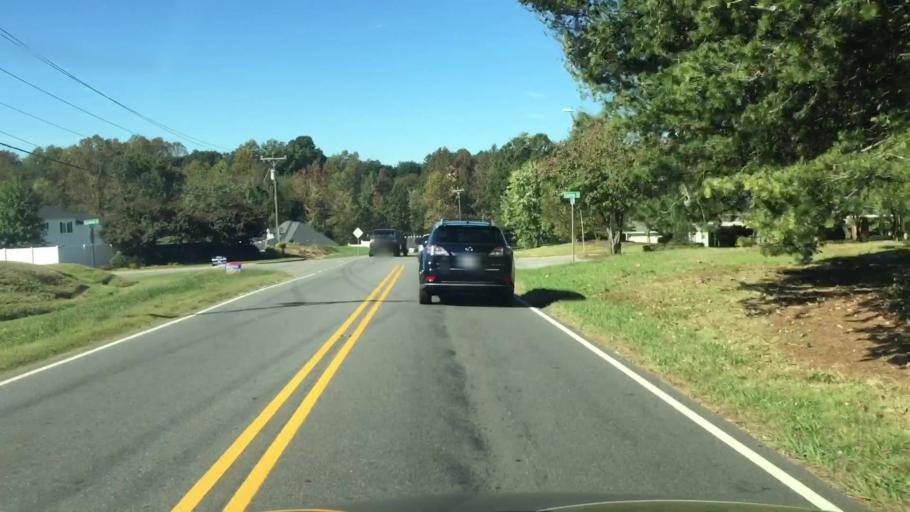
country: US
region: North Carolina
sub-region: Iredell County
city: Mooresville
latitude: 35.5770
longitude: -80.8455
